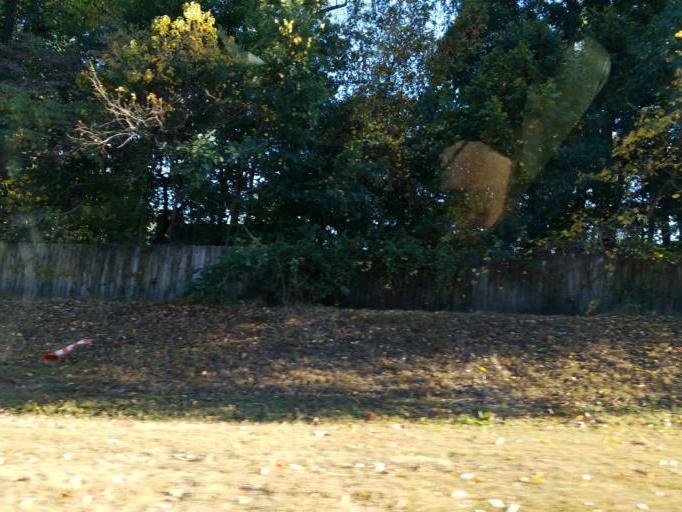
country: US
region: Georgia
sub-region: Fulton County
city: Roswell
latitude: 34.0090
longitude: -84.3834
